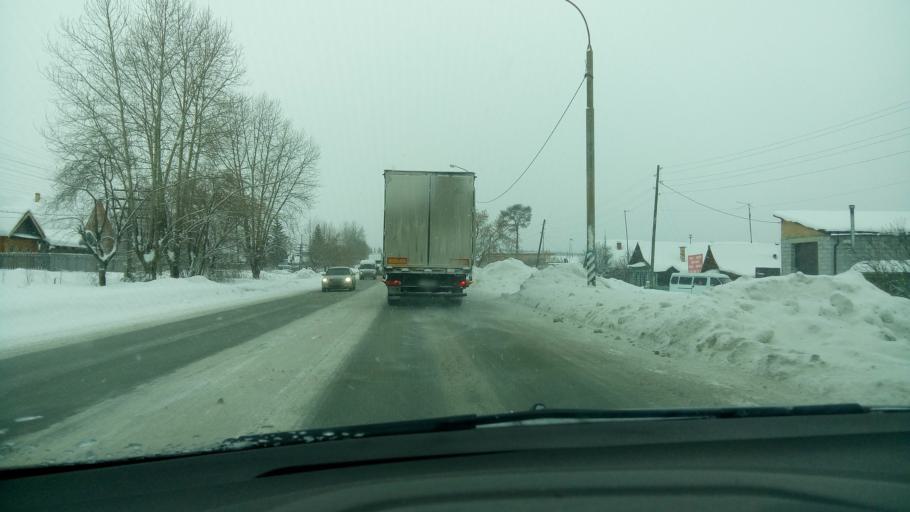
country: RU
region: Sverdlovsk
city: Beloyarskiy
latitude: 56.7572
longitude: 61.3654
